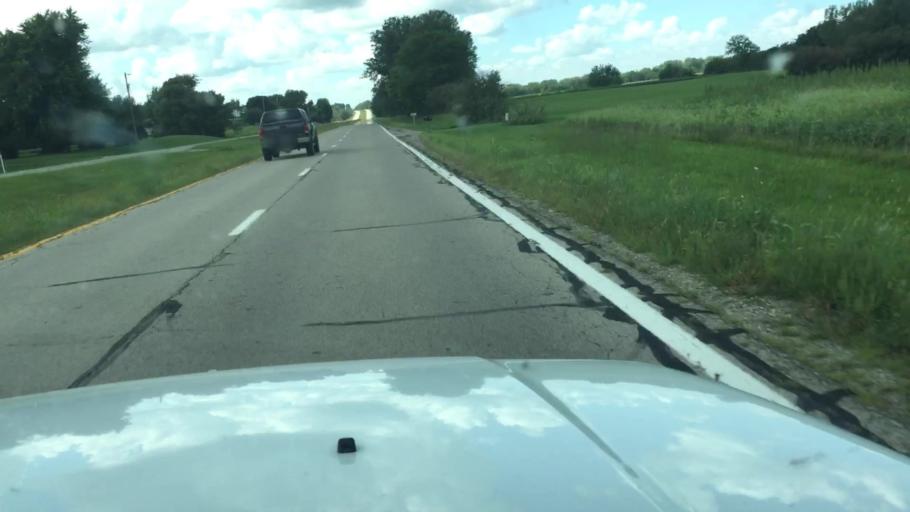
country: US
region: Ohio
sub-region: Madison County
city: Choctaw Lake
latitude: 39.9329
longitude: -83.5107
